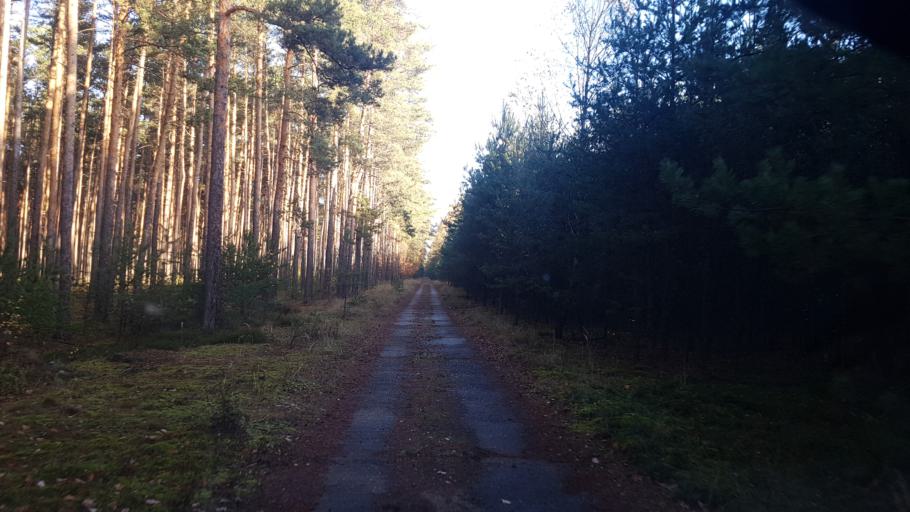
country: DE
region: Brandenburg
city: Crinitz
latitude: 51.7183
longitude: 13.7443
